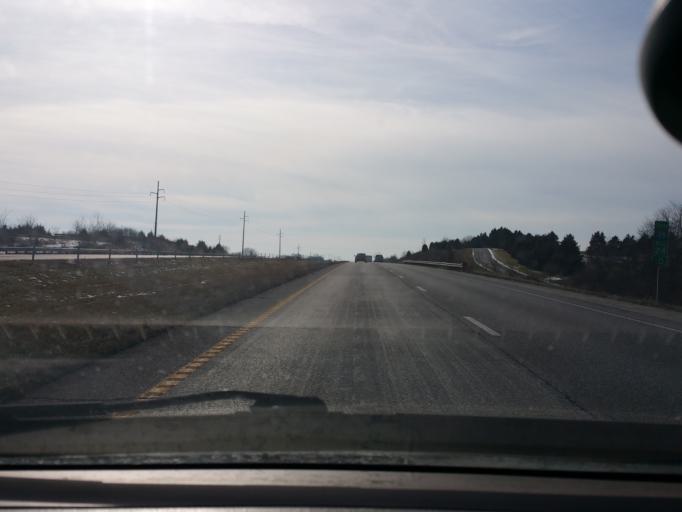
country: US
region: Missouri
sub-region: Clay County
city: Kearney
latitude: 39.3397
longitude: -94.3876
